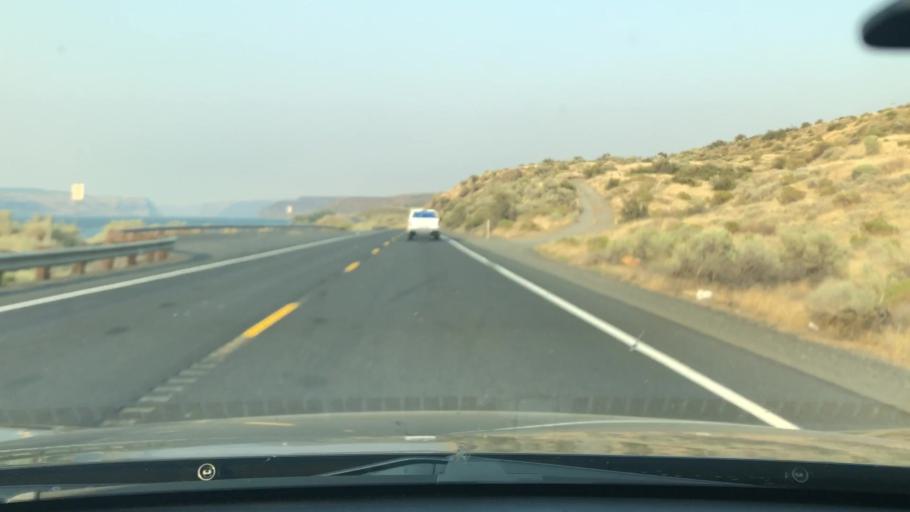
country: US
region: Oregon
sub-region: Umatilla County
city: Stanfield
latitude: 45.9227
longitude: -119.1158
